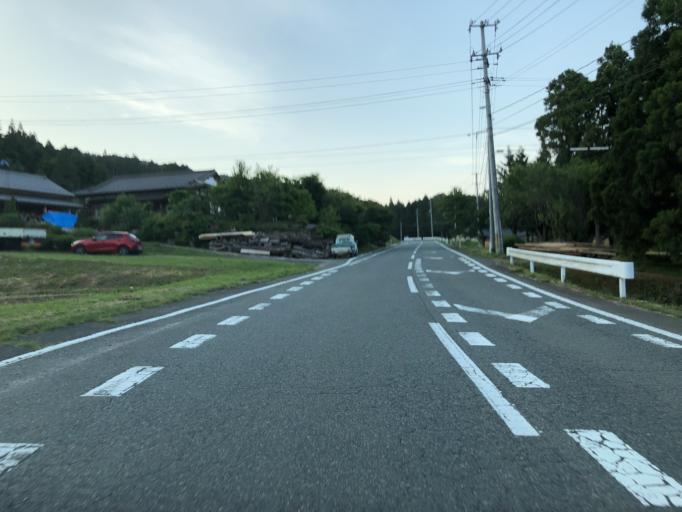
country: JP
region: Fukushima
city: Iwaki
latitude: 37.2445
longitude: 140.9660
